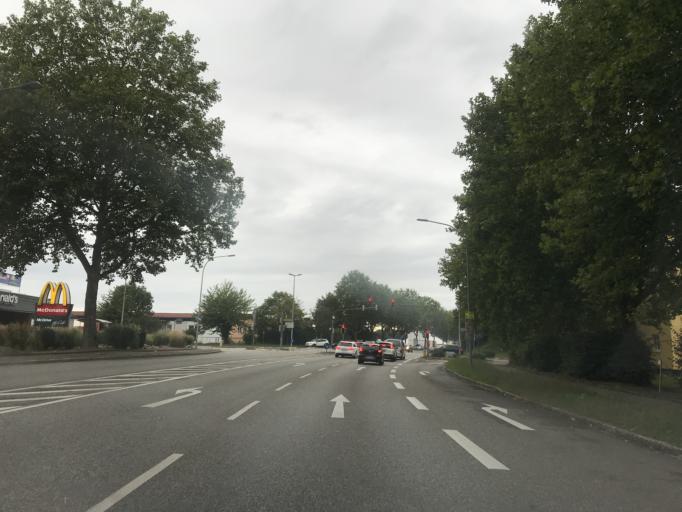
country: CH
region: Aargau
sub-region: Bezirk Rheinfelden
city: Mumpf
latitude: 47.5543
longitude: 7.9314
